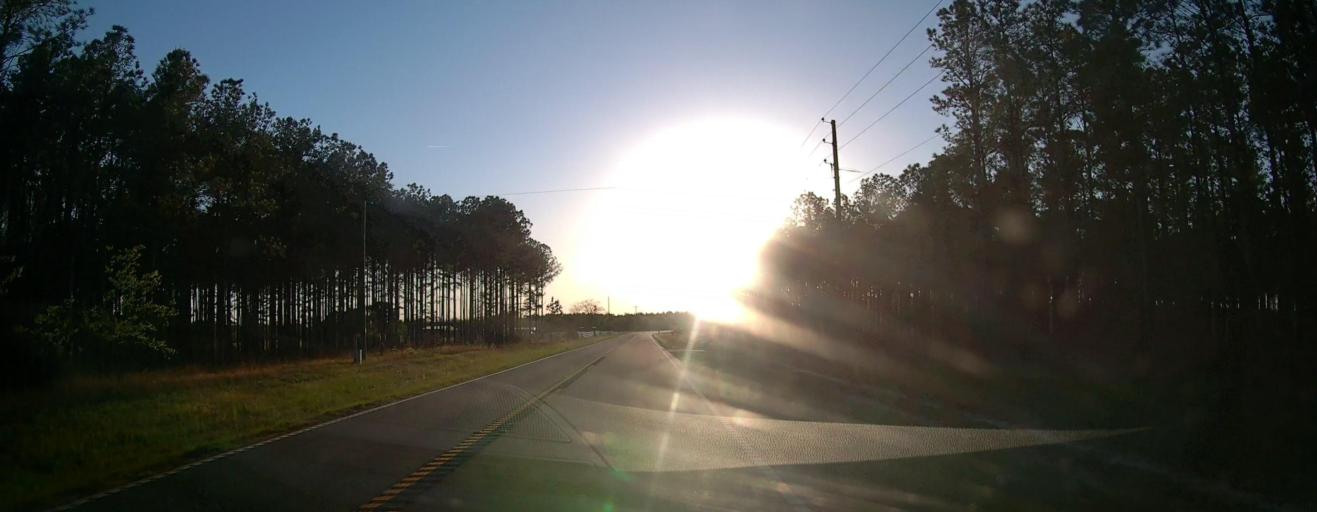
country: US
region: Georgia
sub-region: Talbot County
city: Talbotton
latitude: 32.5370
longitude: -84.5045
